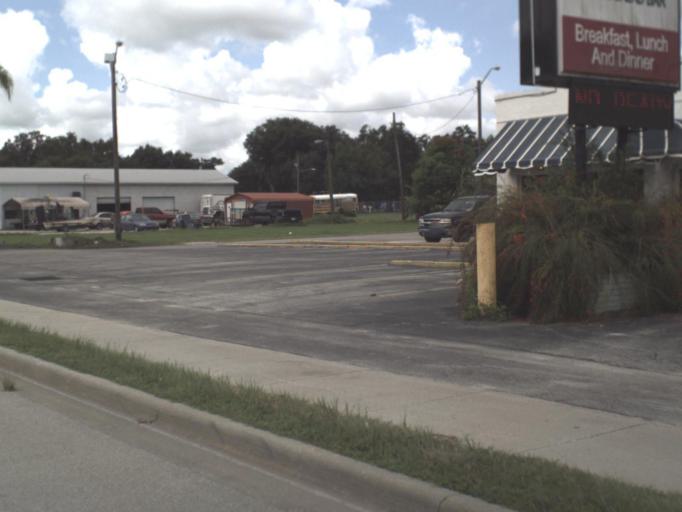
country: US
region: Florida
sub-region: Hardee County
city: Wauchula
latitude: 27.5536
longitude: -81.8130
